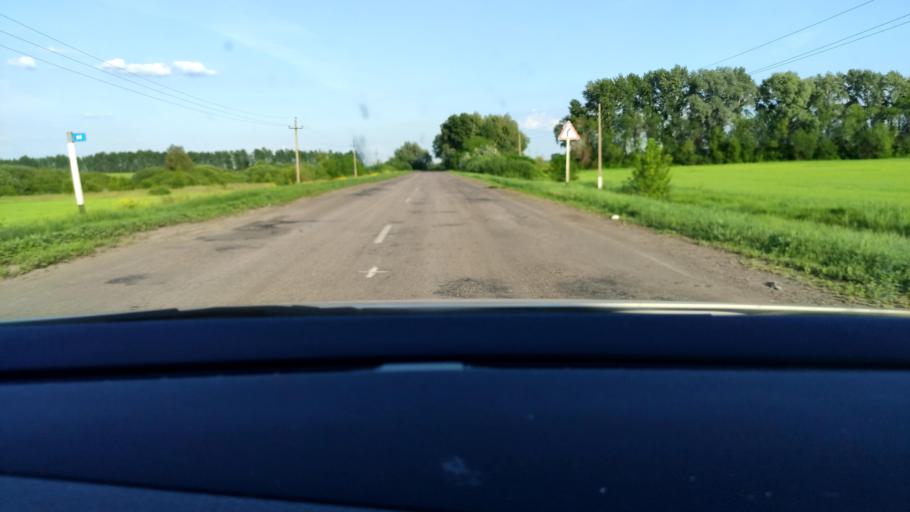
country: RU
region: Voronezj
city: Kashirskoye
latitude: 51.4917
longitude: 39.8466
